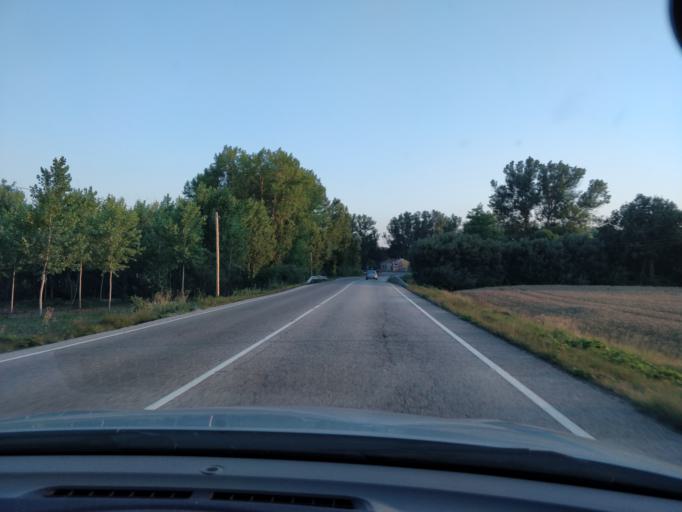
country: ES
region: Castille and Leon
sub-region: Provincia de Burgos
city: Medina de Pomar
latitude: 42.9667
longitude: -3.5468
